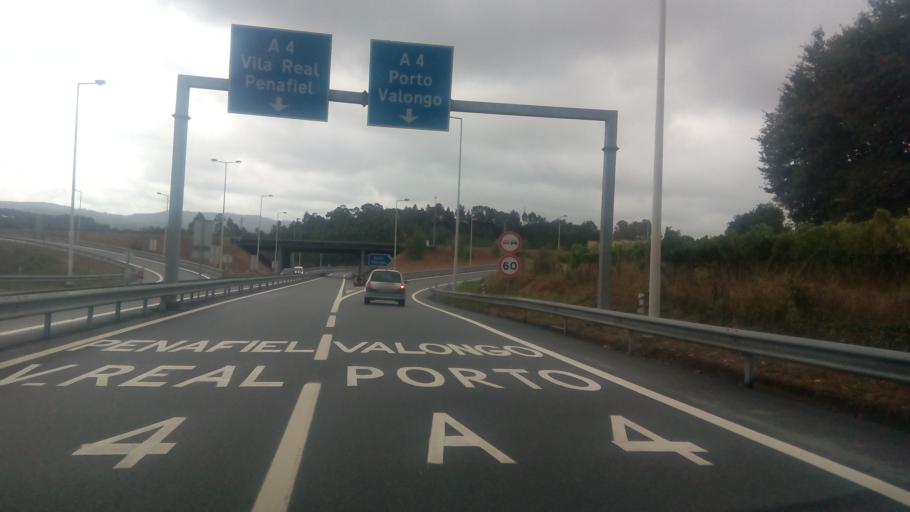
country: PT
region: Porto
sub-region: Paredes
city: Casteloes de Cepeda
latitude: 41.2008
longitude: -8.3381
